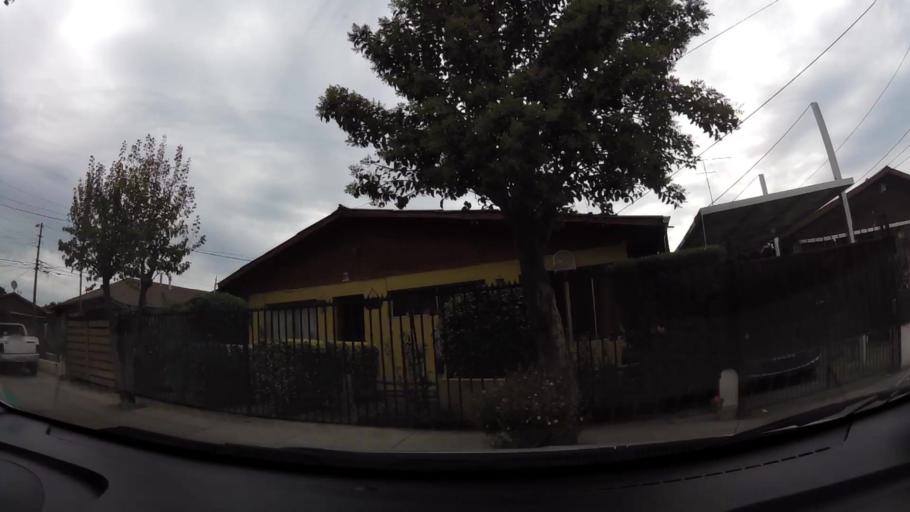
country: CL
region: O'Higgins
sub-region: Provincia de Cachapoal
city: Rancagua
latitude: -34.1620
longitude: -70.7371
